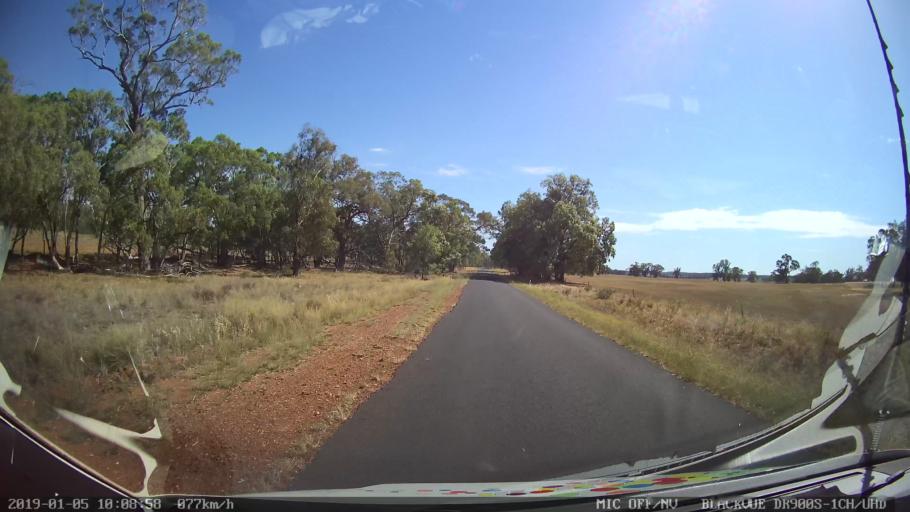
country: AU
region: New South Wales
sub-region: Gilgandra
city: Gilgandra
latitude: -31.6360
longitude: 148.8834
